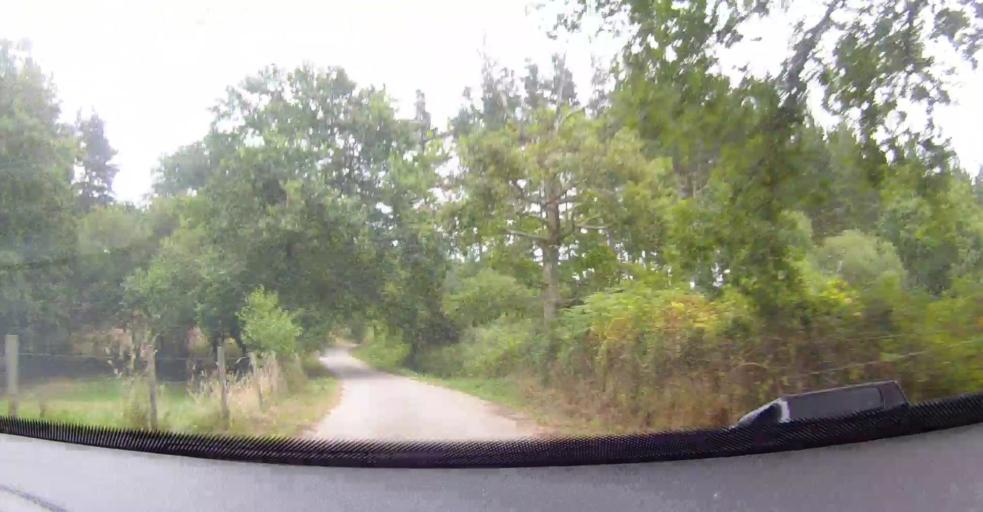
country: ES
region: Basque Country
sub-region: Bizkaia
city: Urrestieta
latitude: 43.2324
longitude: -3.1806
